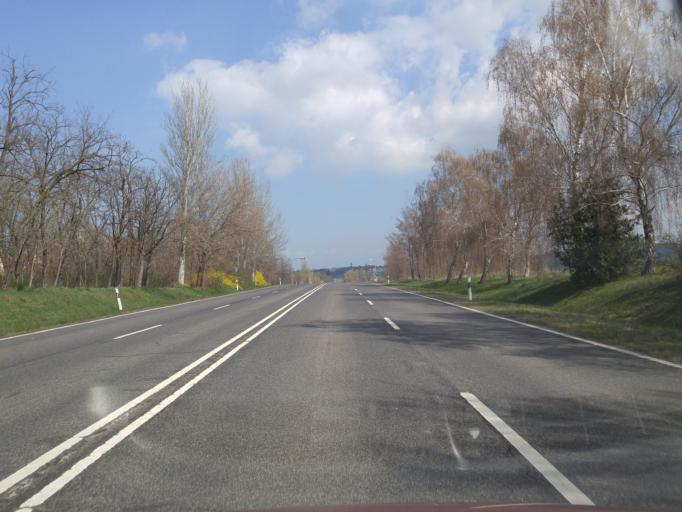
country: HU
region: Somogy
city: Balatonszarszo
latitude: 46.8307
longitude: 17.8440
